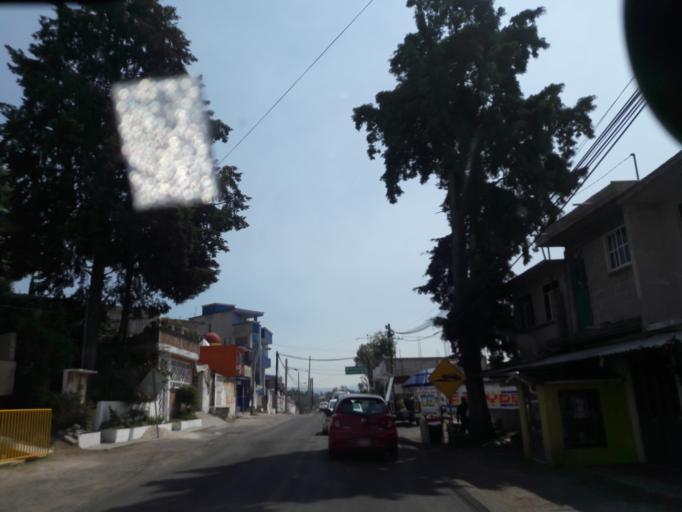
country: MX
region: Tlaxcala
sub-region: Ixtacuixtla de Mariano Matamoros
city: Villa Mariano Matamoros
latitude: 19.3145
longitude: -98.3891
